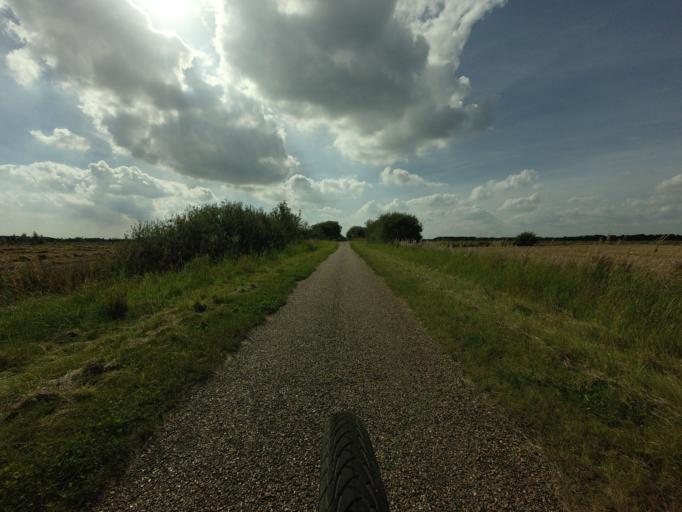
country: DK
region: Central Jutland
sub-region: Herning Kommune
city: Sunds
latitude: 56.2211
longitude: 9.0611
